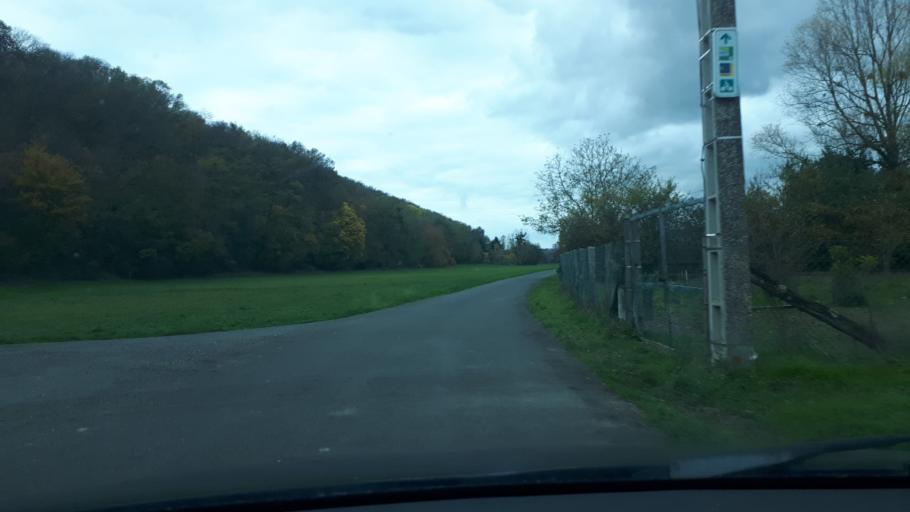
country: FR
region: Centre
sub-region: Departement du Loir-et-Cher
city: Lunay
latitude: 47.7722
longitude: 0.9238
